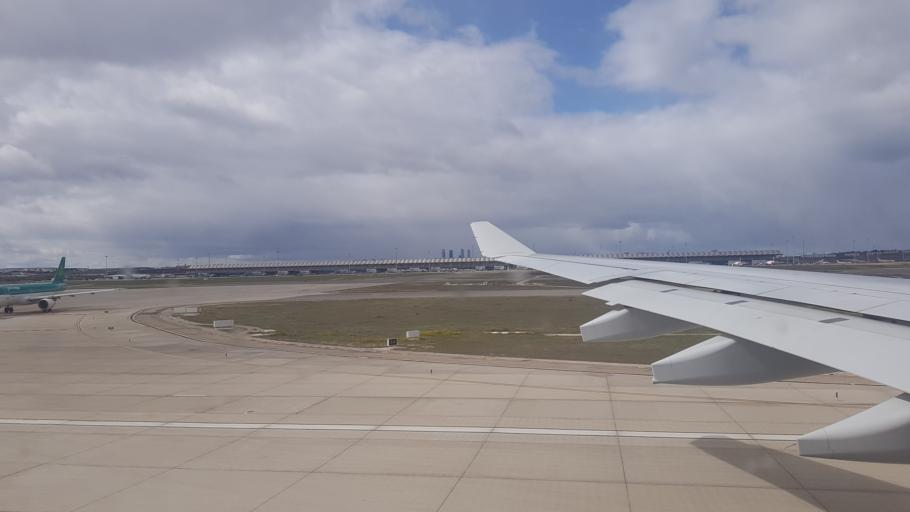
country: ES
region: Madrid
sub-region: Provincia de Madrid
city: Barajas de Madrid
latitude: 40.4933
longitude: -3.5744
